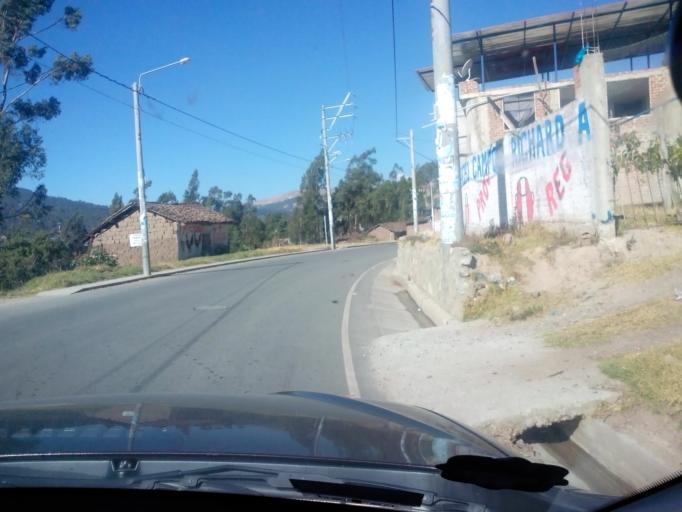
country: PE
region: Apurimac
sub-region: Provincia de Andahuaylas
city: Talavera
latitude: -13.6583
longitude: -73.4403
